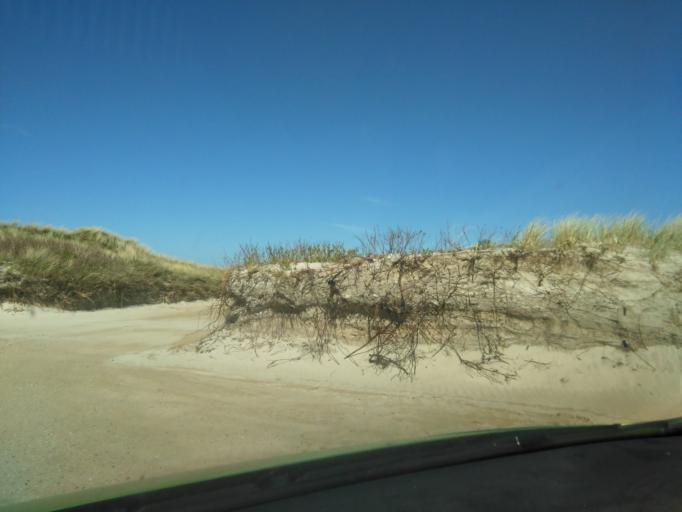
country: DK
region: South Denmark
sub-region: Varde Kommune
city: Oksbol
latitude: 55.4965
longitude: 8.2579
